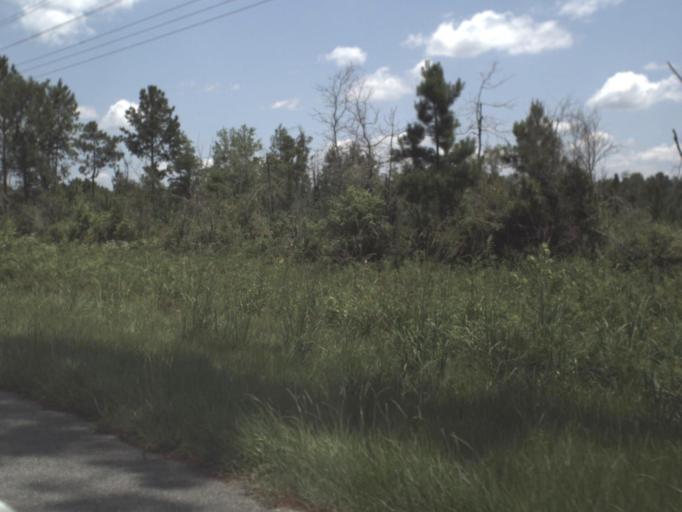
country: US
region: Florida
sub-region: Madison County
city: Madison
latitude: 30.4980
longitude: -83.6317
